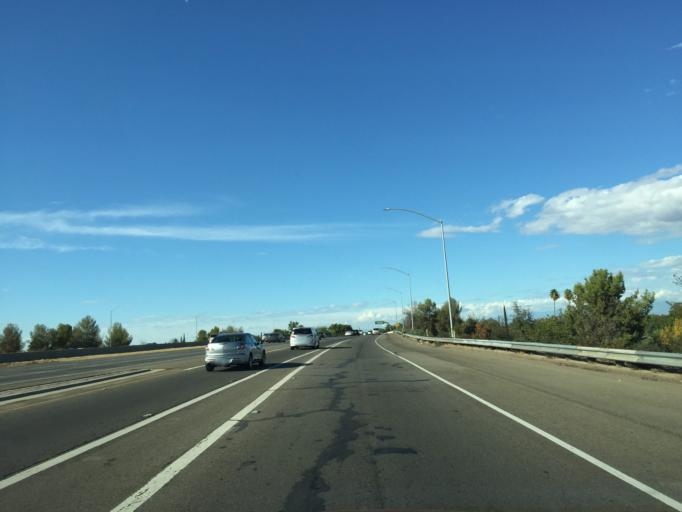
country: US
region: California
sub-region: Fresno County
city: Fresno
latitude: 36.7585
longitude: -119.7752
